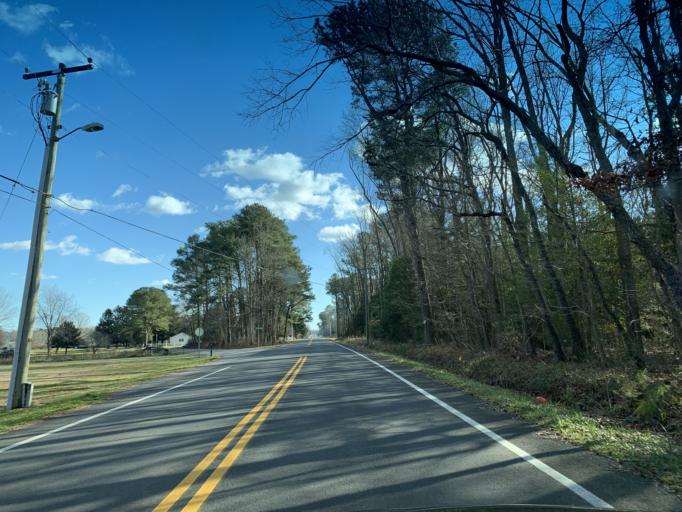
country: US
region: Maryland
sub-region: Worcester County
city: Berlin
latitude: 38.3611
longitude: -75.2001
